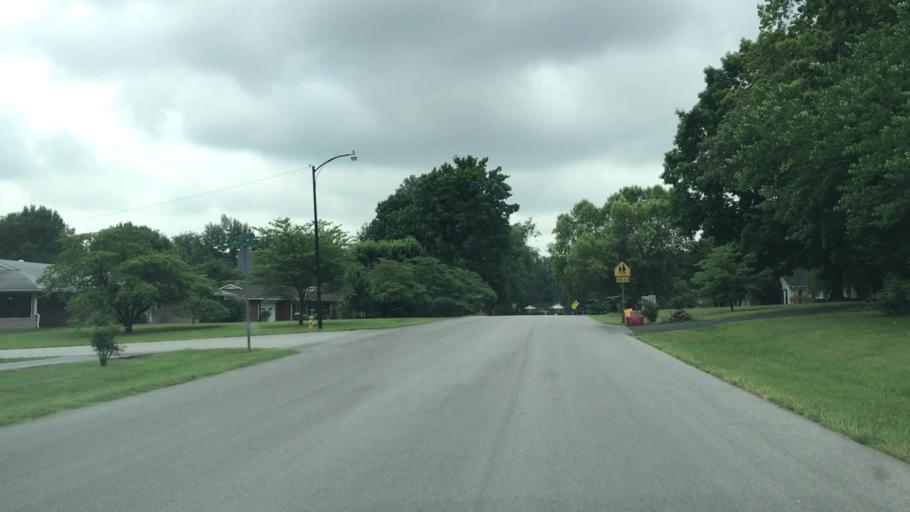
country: US
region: Kentucky
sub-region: Warren County
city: Bowling Green
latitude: 36.9874
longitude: -86.4155
